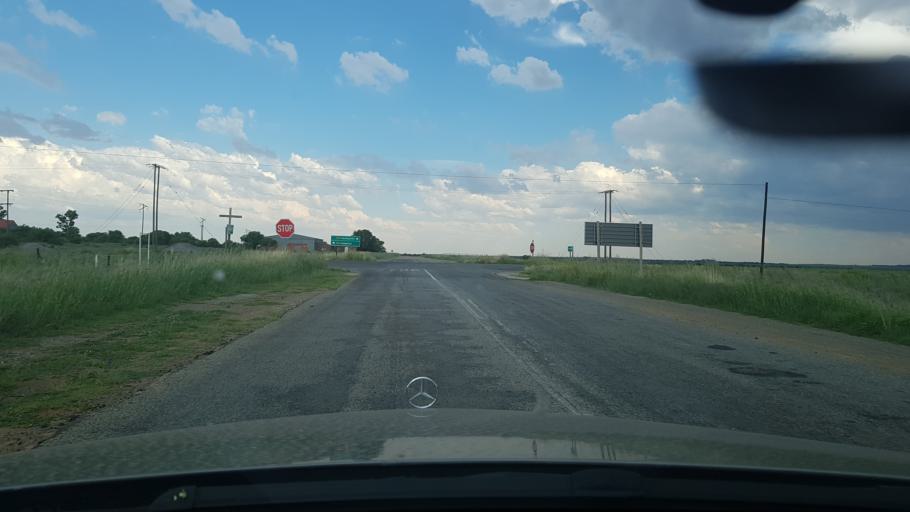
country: ZA
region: Orange Free State
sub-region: Lejweleputswa District Municipality
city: Hoopstad
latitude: -27.9544
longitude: 25.7033
